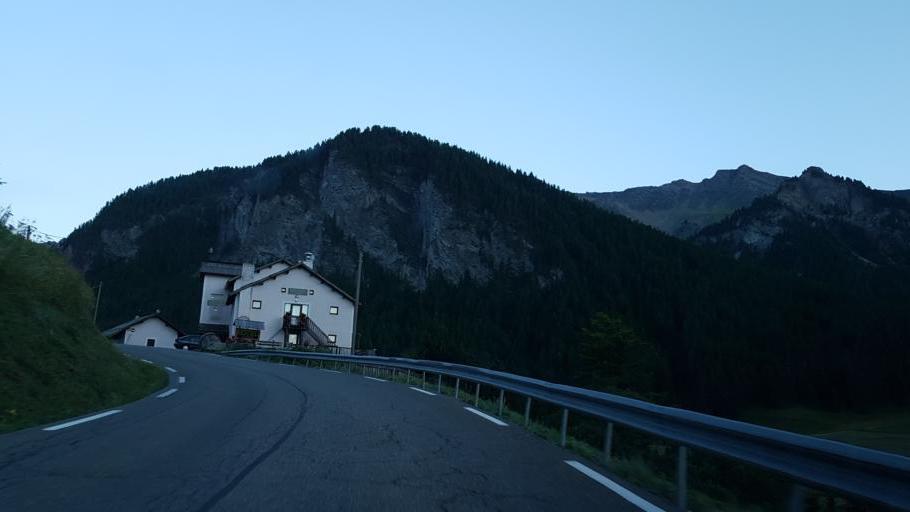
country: IT
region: Piedmont
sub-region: Provincia di Cuneo
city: Pontechianale
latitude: 44.7018
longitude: 6.8587
